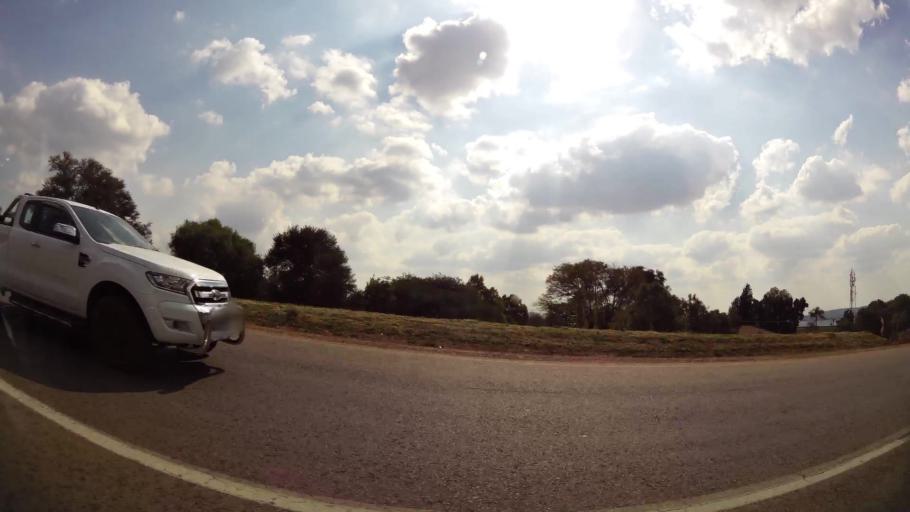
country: ZA
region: Gauteng
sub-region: City of Tshwane Metropolitan Municipality
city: Centurion
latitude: -25.8052
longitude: 28.2939
